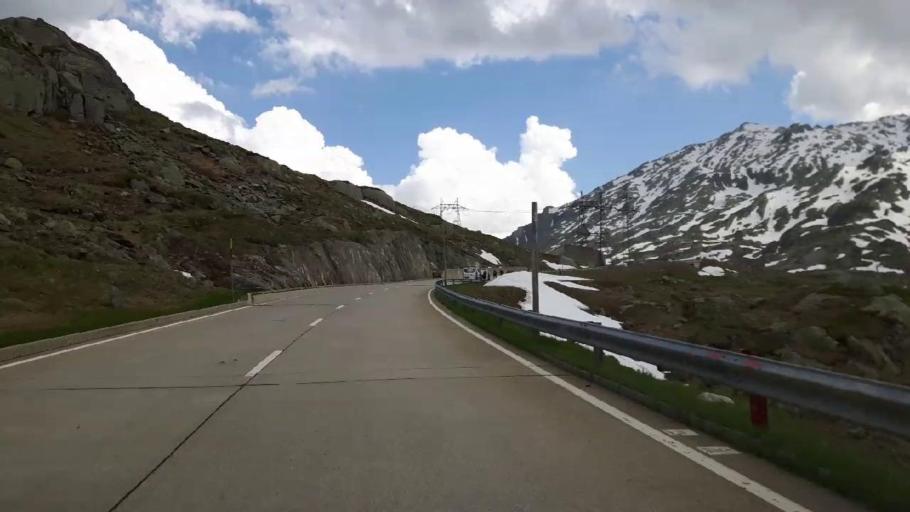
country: CH
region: Ticino
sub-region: Leventina District
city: Airolo
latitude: 46.5659
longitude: 8.5607
